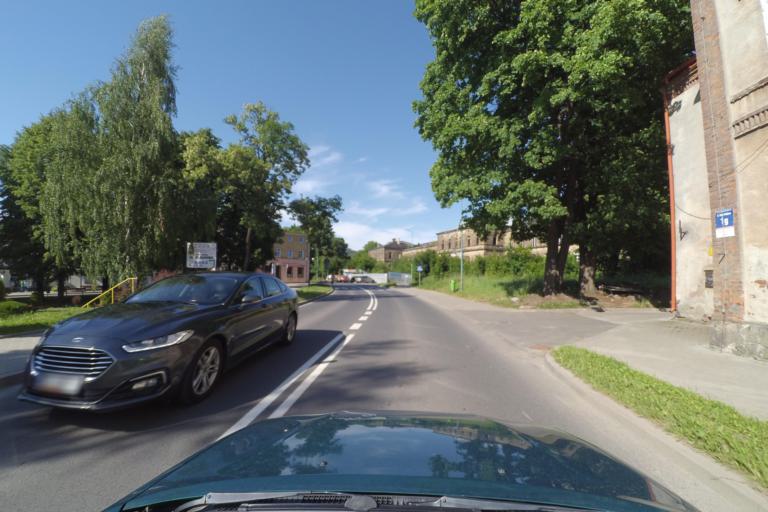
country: PL
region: Lower Silesian Voivodeship
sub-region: Powiat kamiennogorski
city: Lubawka
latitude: 50.7059
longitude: 16.0018
